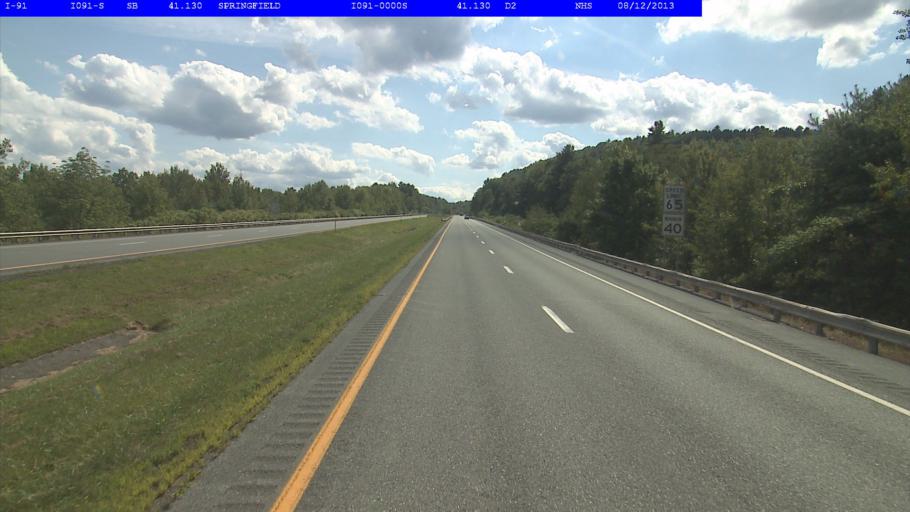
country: US
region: New Hampshire
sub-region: Sullivan County
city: Charlestown
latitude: 43.2596
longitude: -72.4371
